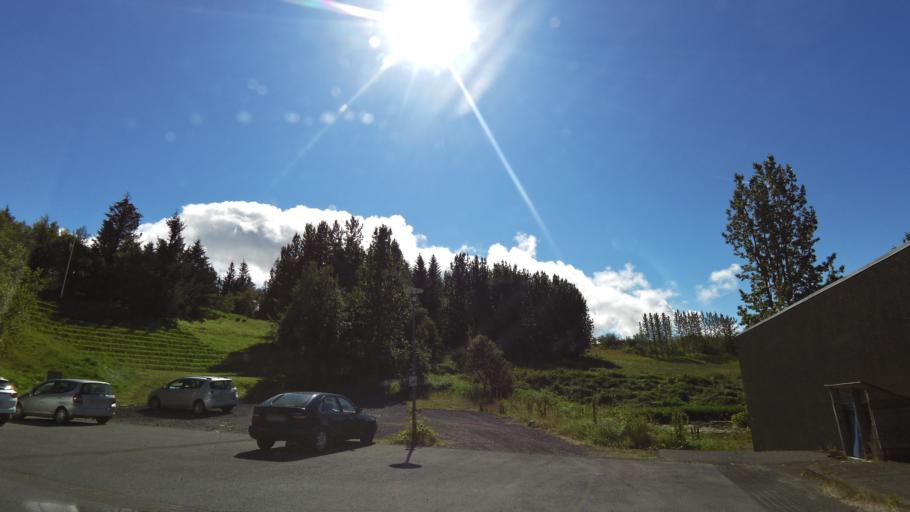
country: IS
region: Capital Region
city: Mosfellsbaer
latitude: 64.1668
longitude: -21.6781
